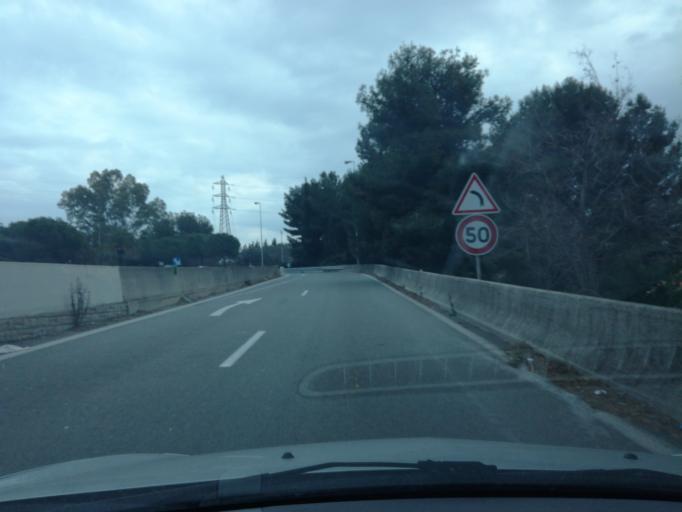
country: FR
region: Provence-Alpes-Cote d'Azur
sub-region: Departement des Alpes-Maritimes
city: Mougins
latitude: 43.5851
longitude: 7.0035
